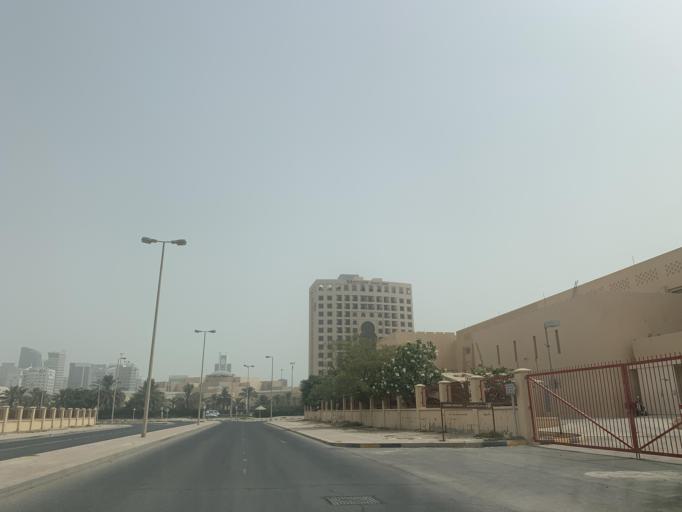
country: BH
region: Manama
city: Jidd Hafs
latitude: 26.2298
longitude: 50.5405
